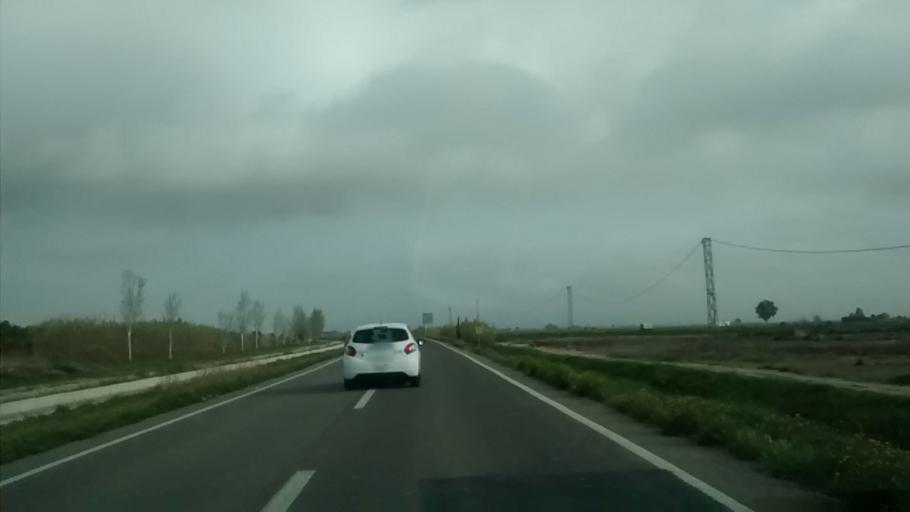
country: ES
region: Catalonia
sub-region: Provincia de Tarragona
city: Sant Carles de la Rapita
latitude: 40.6380
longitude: 0.6016
